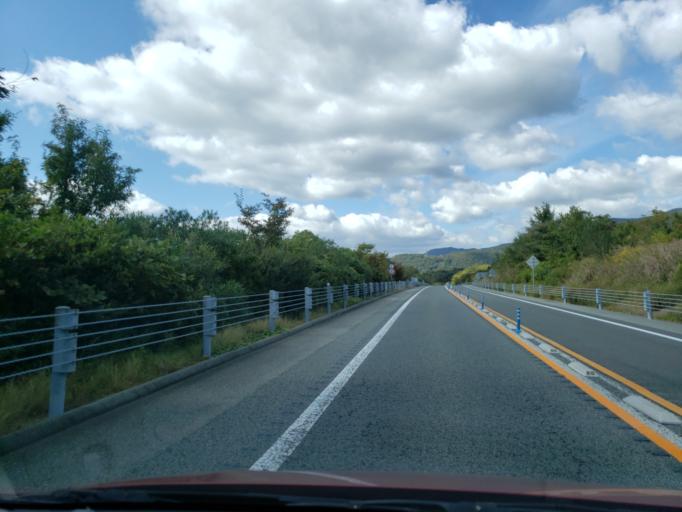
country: JP
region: Tokushima
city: Kamojimacho-jogejima
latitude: 34.1216
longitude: 134.3684
